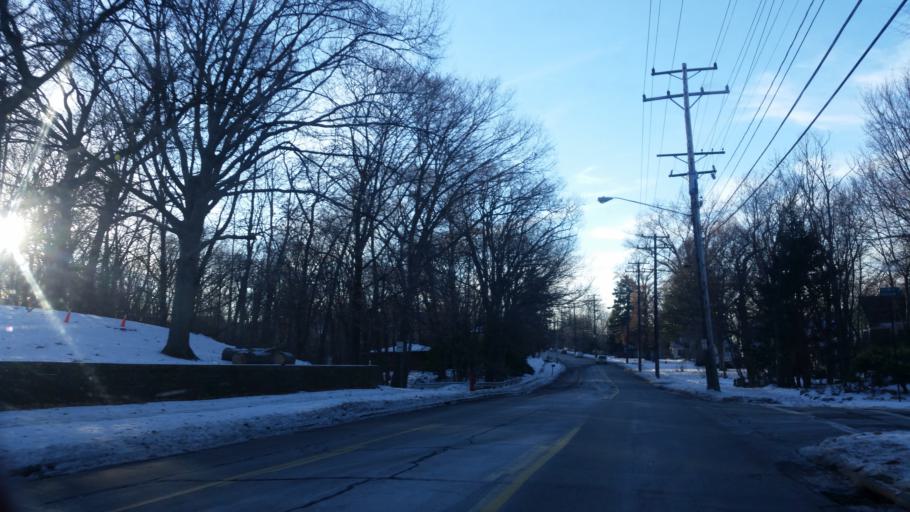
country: US
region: Ohio
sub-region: Cuyahoga County
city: Rocky River
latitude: 41.4717
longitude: -81.8642
